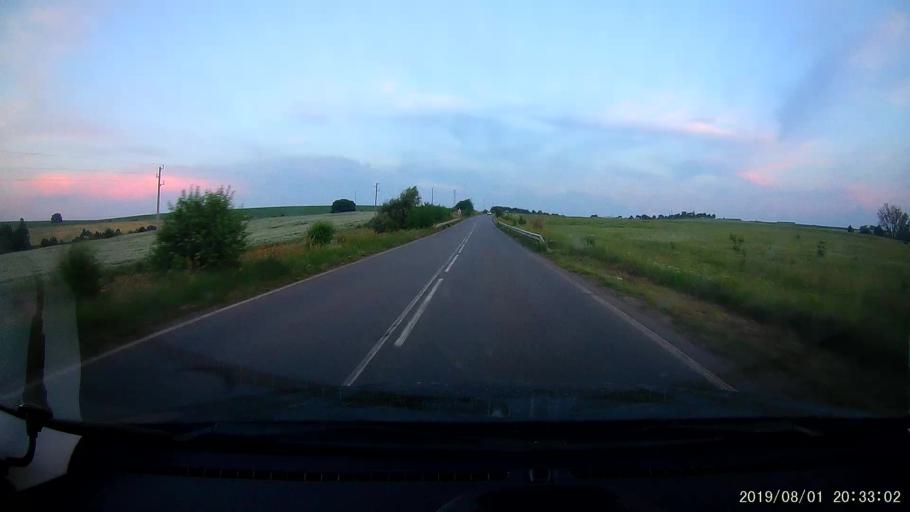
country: BG
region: Yambol
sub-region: Obshtina Elkhovo
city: Elkhovo
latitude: 42.1125
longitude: 26.5312
